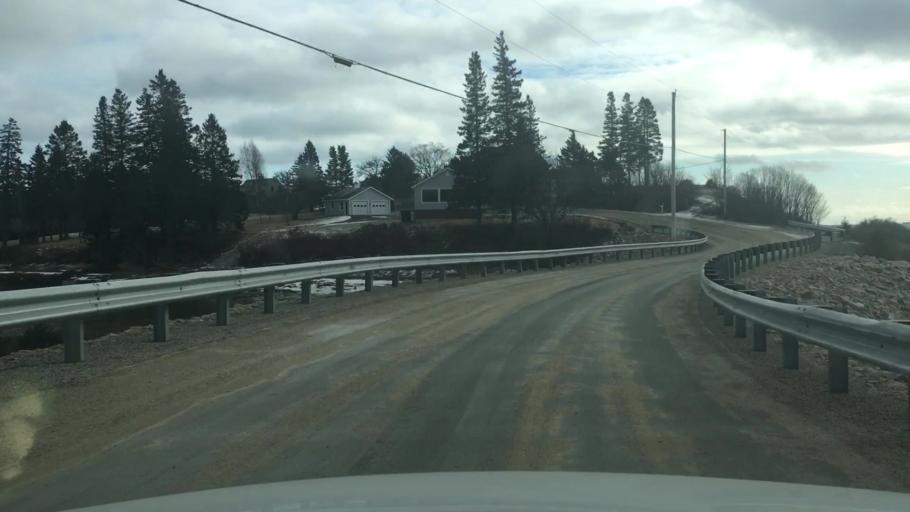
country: US
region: Maine
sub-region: Washington County
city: Machias
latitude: 44.6100
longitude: -67.4767
